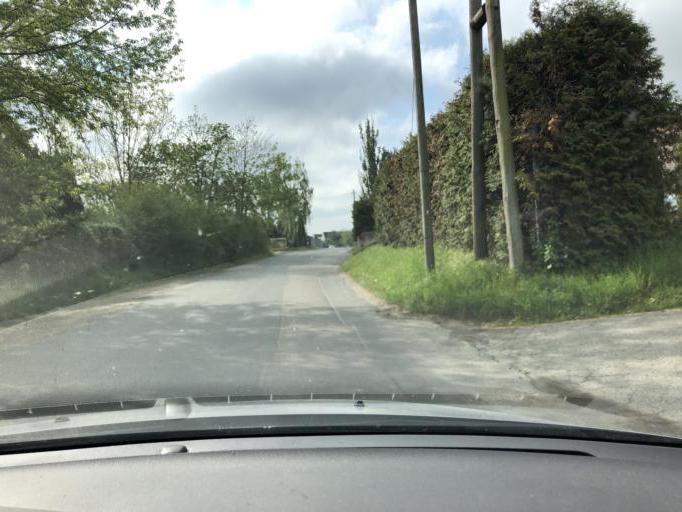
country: DE
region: Thuringia
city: Gerstenberg
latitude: 51.0155
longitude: 12.4370
